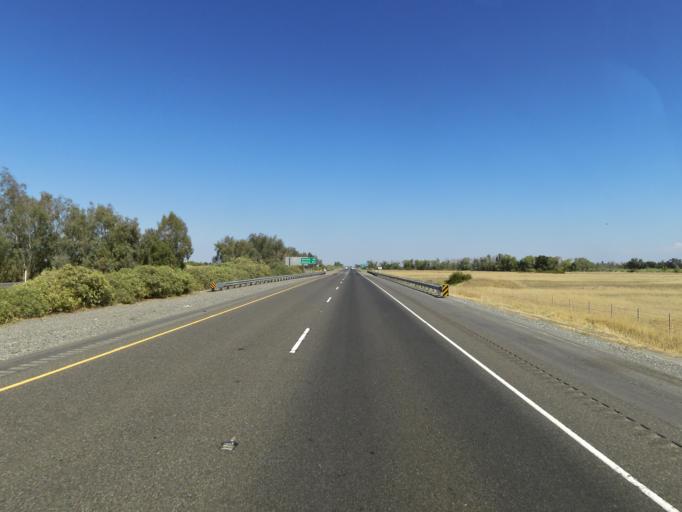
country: US
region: California
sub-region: Glenn County
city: Orland
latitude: 39.7629
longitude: -122.2051
